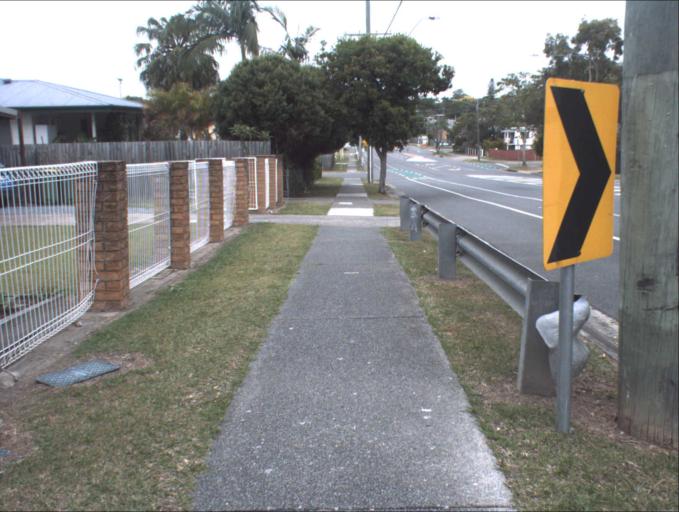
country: AU
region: Queensland
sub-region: Logan
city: Logan City
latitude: -27.6517
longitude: 153.1109
